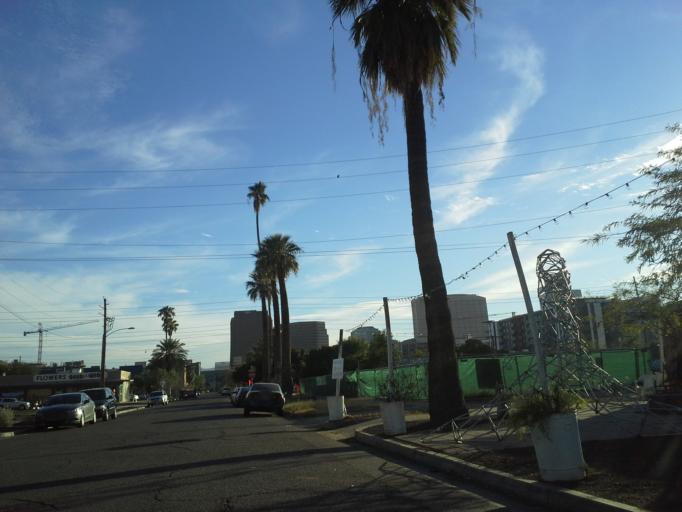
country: US
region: Arizona
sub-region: Maricopa County
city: Phoenix
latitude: 33.4595
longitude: -112.0675
